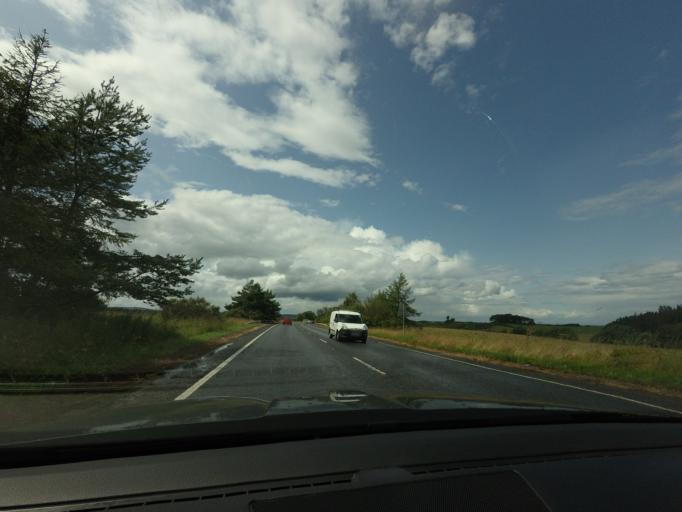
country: GB
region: Scotland
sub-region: Moray
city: Lhanbryd
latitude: 57.6340
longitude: -3.2269
